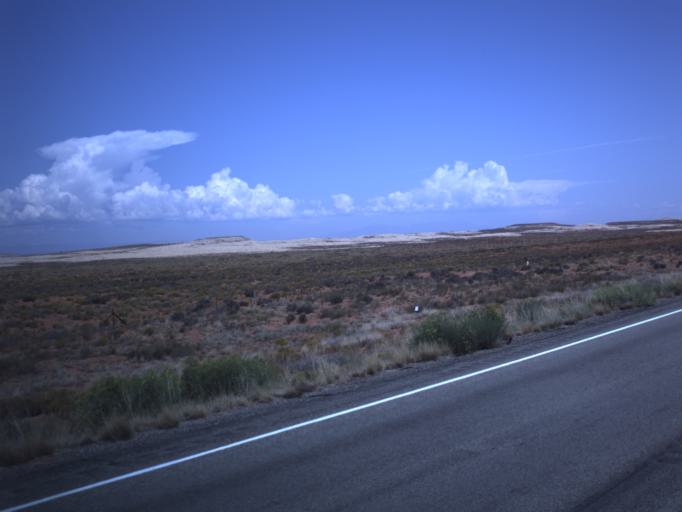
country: US
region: Utah
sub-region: San Juan County
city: Blanding
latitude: 37.0235
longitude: -109.6036
